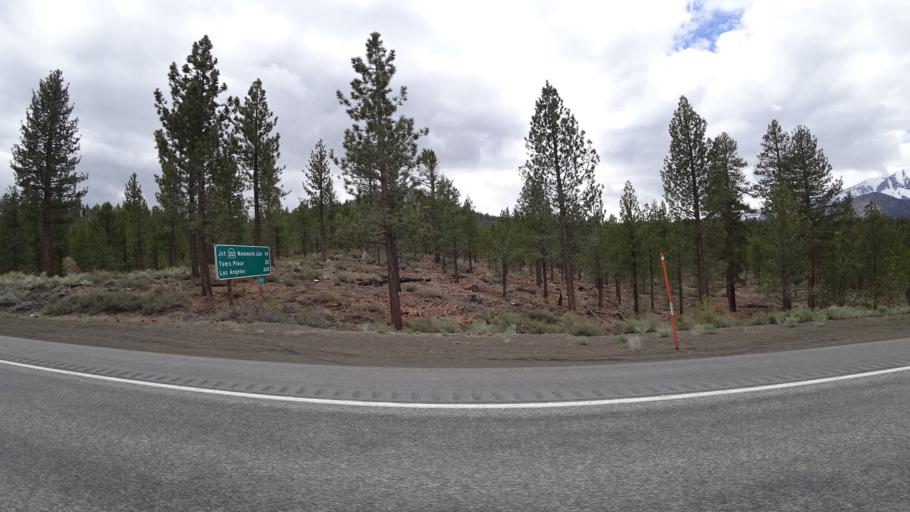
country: US
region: California
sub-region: Mono County
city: Mammoth Lakes
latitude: 37.8063
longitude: -119.0449
